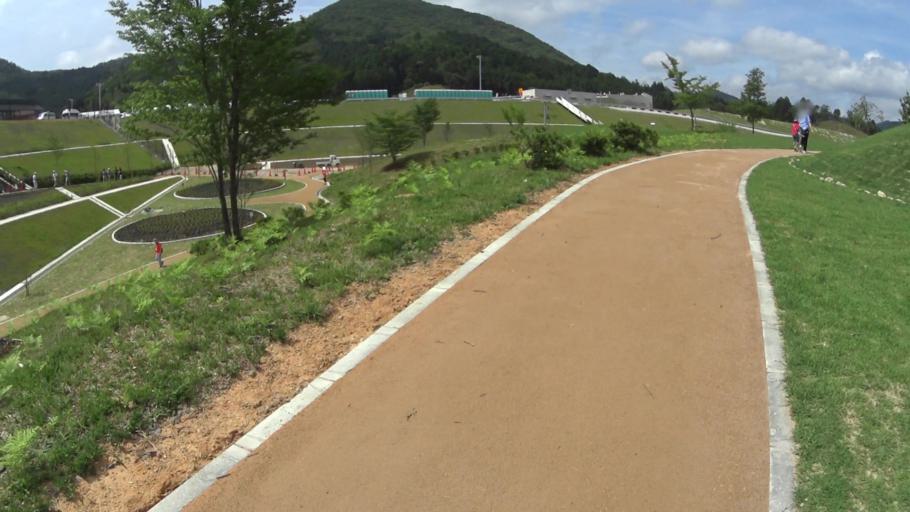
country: JP
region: Kyoto
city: Ayabe
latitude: 35.1576
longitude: 135.4156
